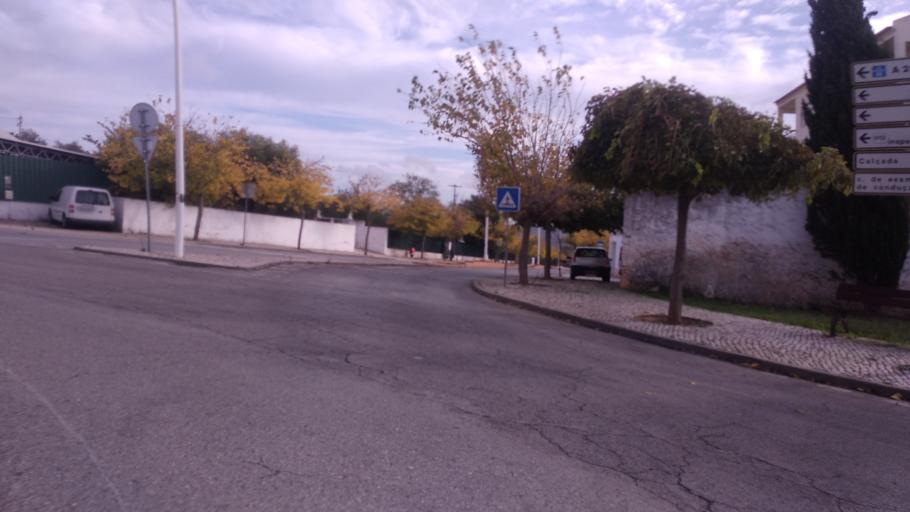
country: PT
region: Faro
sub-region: Sao Bras de Alportel
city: Sao Bras de Alportel
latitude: 37.1508
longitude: -7.8936
